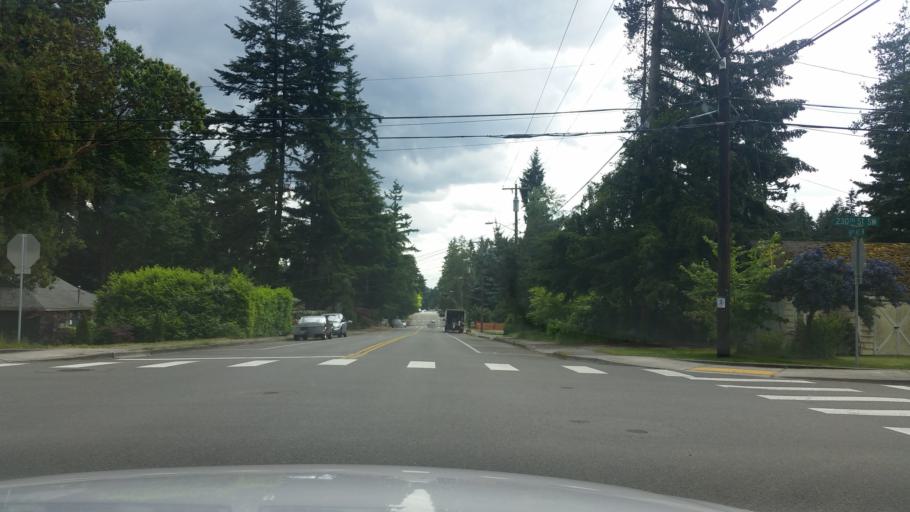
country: US
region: Washington
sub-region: Snohomish County
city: Mountlake Terrace
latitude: 47.7904
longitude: -122.3112
